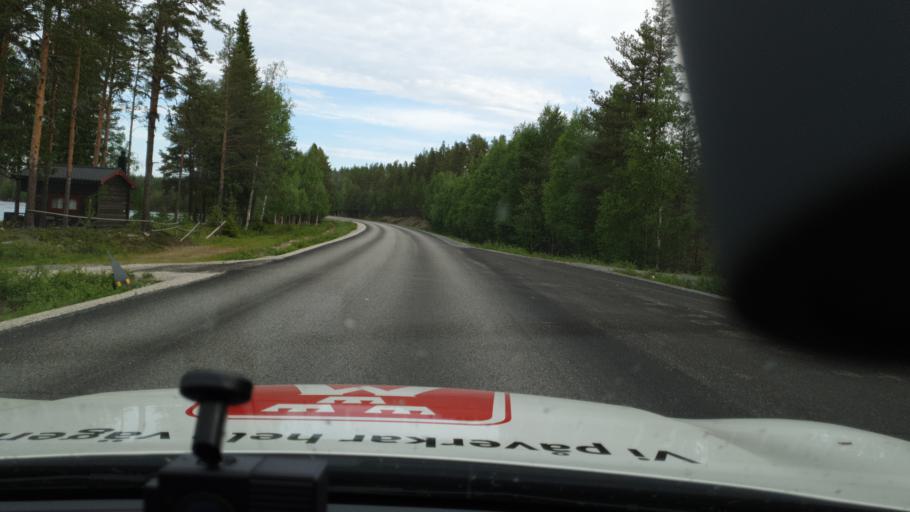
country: SE
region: Vaesterbotten
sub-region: Mala Kommun
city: Mala
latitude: 64.9397
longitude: 18.6249
